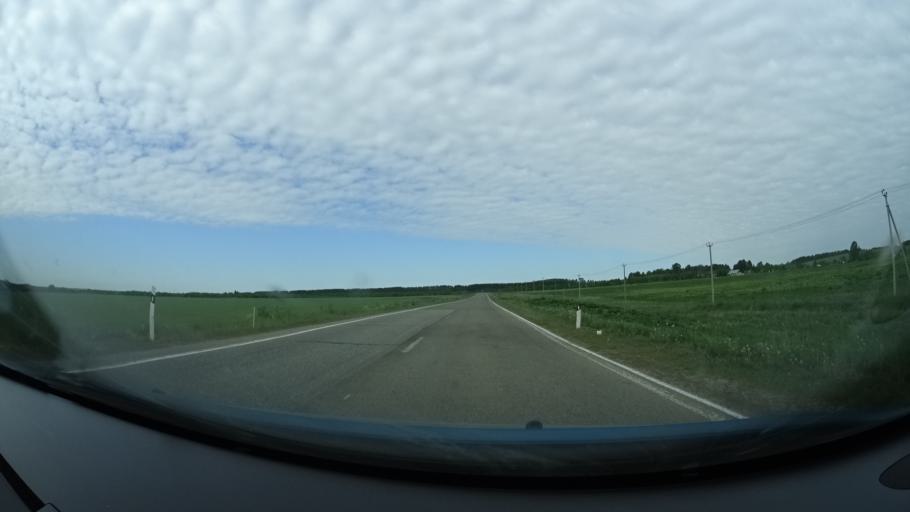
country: RU
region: Perm
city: Kuyeda
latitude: 56.4984
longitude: 55.6144
